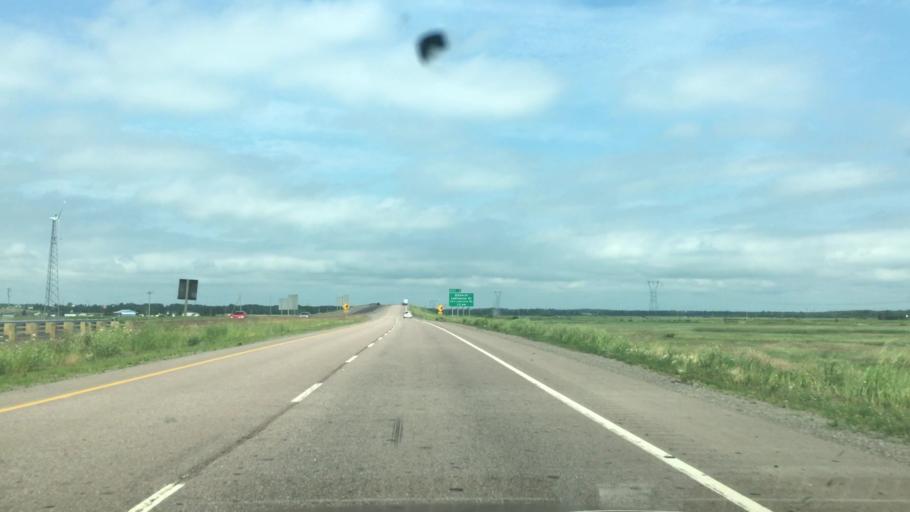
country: CA
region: Nova Scotia
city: Amherst
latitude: 45.8336
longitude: -64.2382
